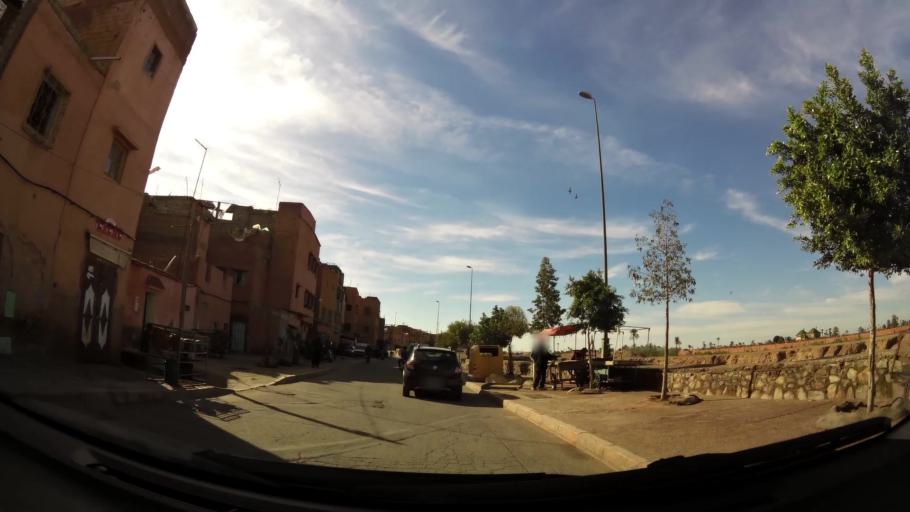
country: MA
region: Marrakech-Tensift-Al Haouz
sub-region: Marrakech
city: Marrakesh
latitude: 31.6164
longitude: -7.9632
